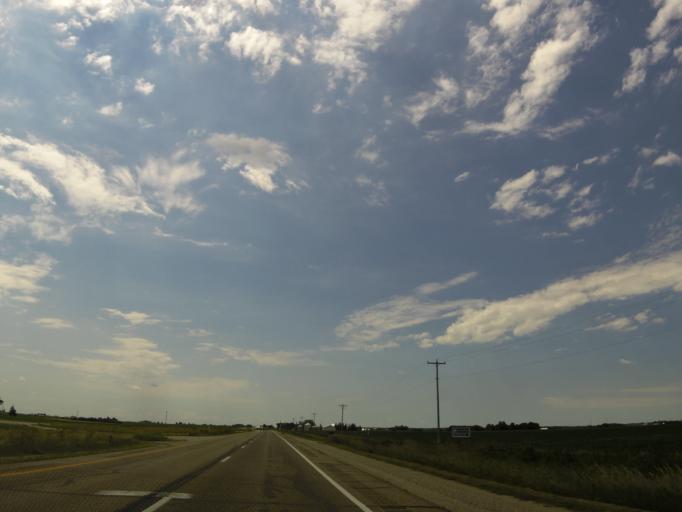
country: US
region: Iowa
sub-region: Bremer County
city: Tripoli
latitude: 42.7671
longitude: -92.3373
